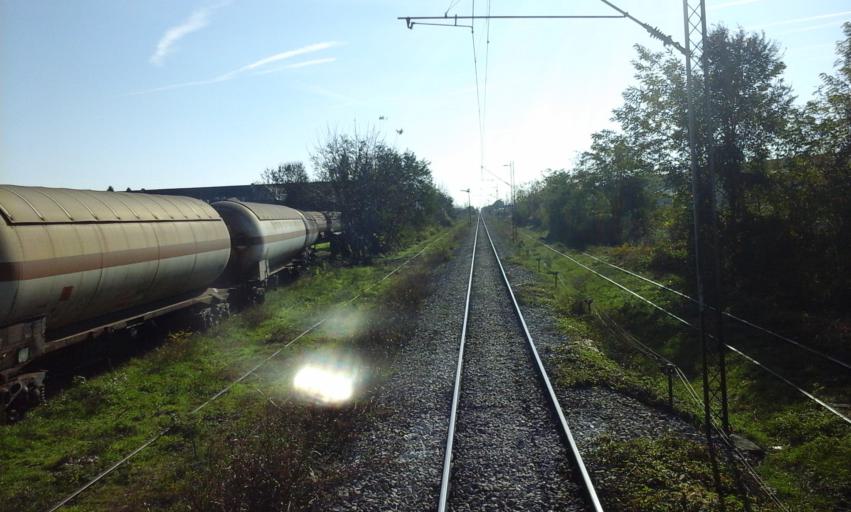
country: RS
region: Autonomna Pokrajina Vojvodina
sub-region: Severnobacki Okrug
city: Subotica
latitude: 46.0650
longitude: 19.6876
